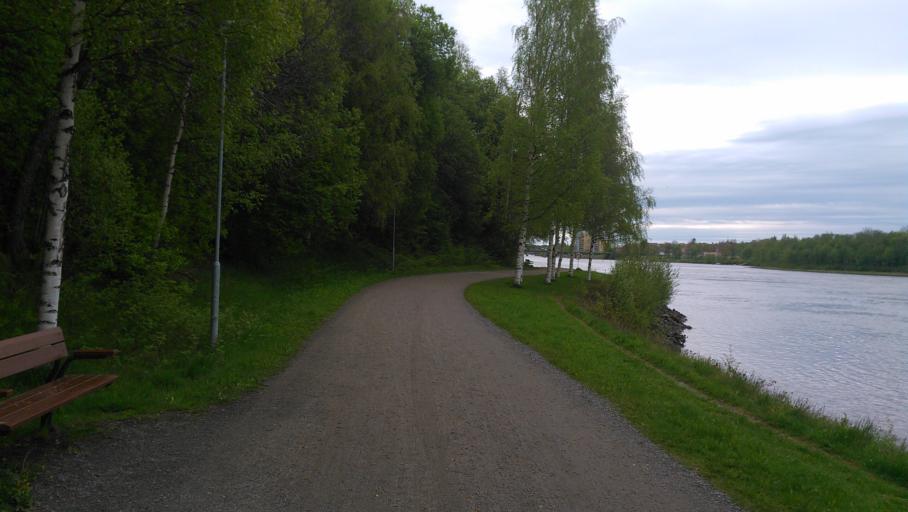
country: SE
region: Vaesterbotten
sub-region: Umea Kommun
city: Umea
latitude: 63.8289
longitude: 20.2306
